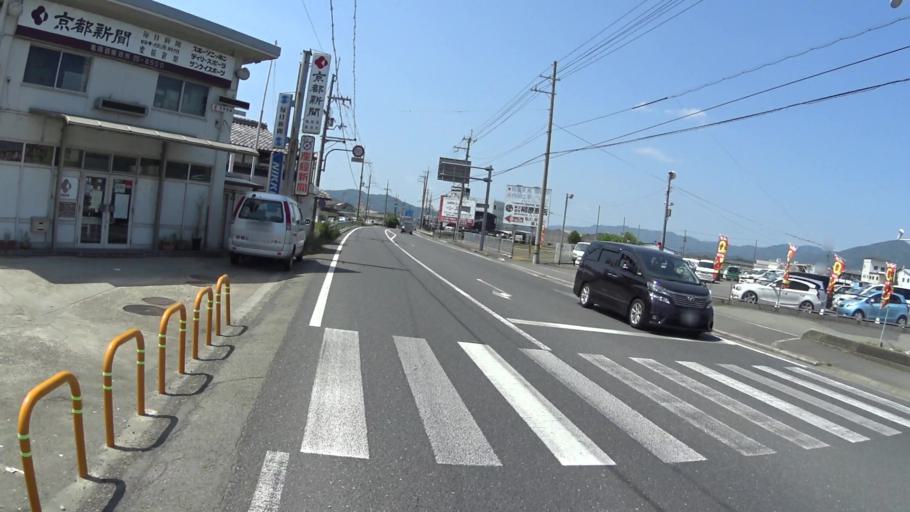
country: JP
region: Kyoto
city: Kameoka
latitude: 35.0179
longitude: 135.5630
